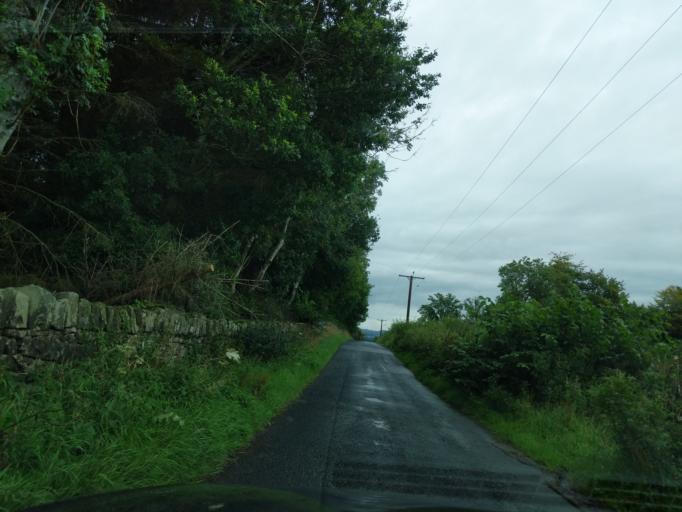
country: GB
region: Scotland
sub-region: Fife
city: Limekilns
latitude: 55.9851
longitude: -3.4646
